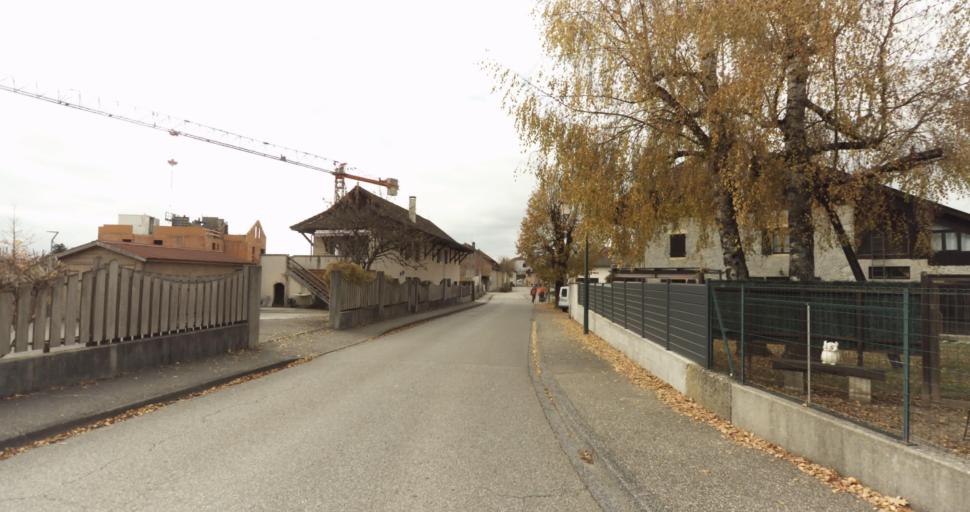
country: FR
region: Rhone-Alpes
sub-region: Departement de la Haute-Savoie
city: Metz-Tessy
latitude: 45.9416
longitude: 6.1081
